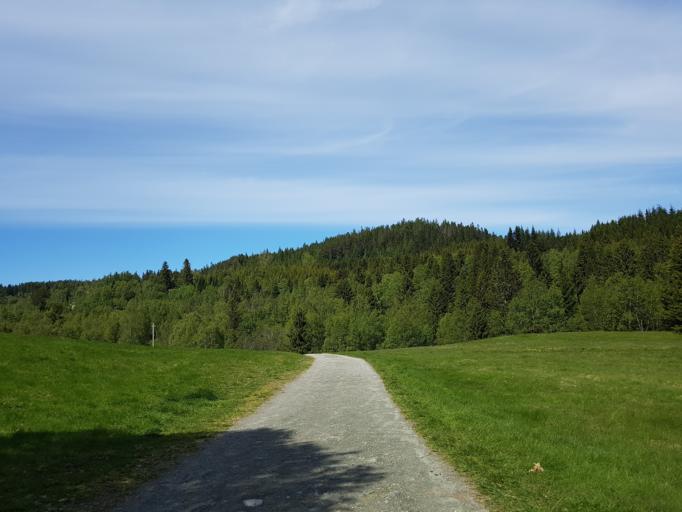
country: NO
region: Sor-Trondelag
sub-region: Trondheim
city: Trondheim
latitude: 63.4191
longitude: 10.3119
